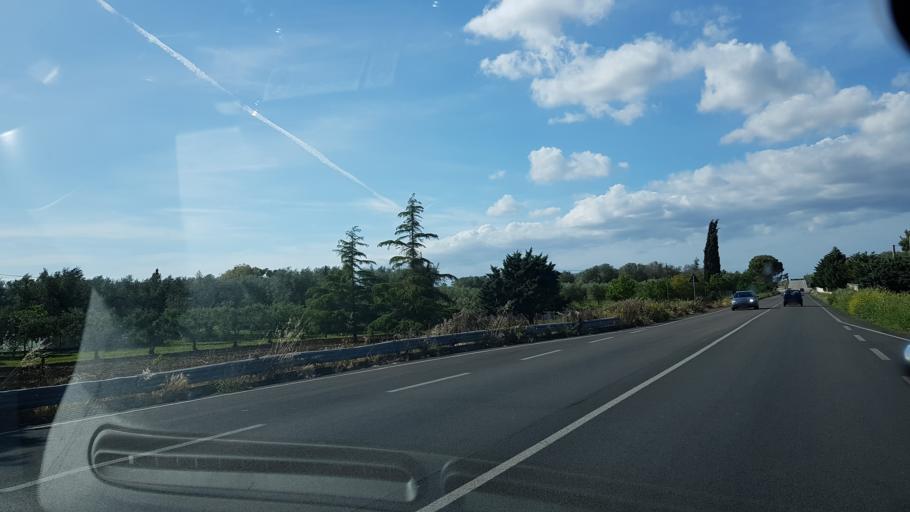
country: IT
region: Apulia
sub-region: Provincia di Brindisi
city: Mesagne
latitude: 40.5629
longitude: 17.7875
